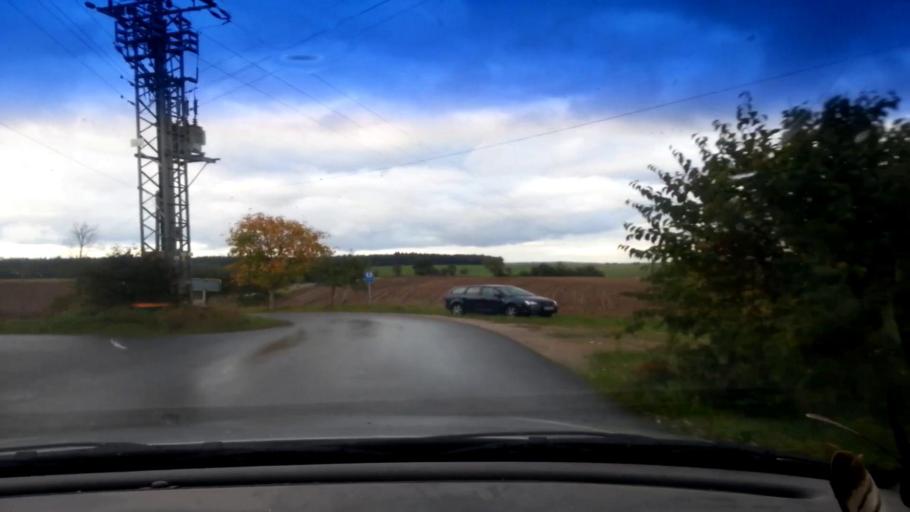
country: DE
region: Bavaria
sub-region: Upper Franconia
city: Burgwindheim
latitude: 49.8022
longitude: 10.6299
